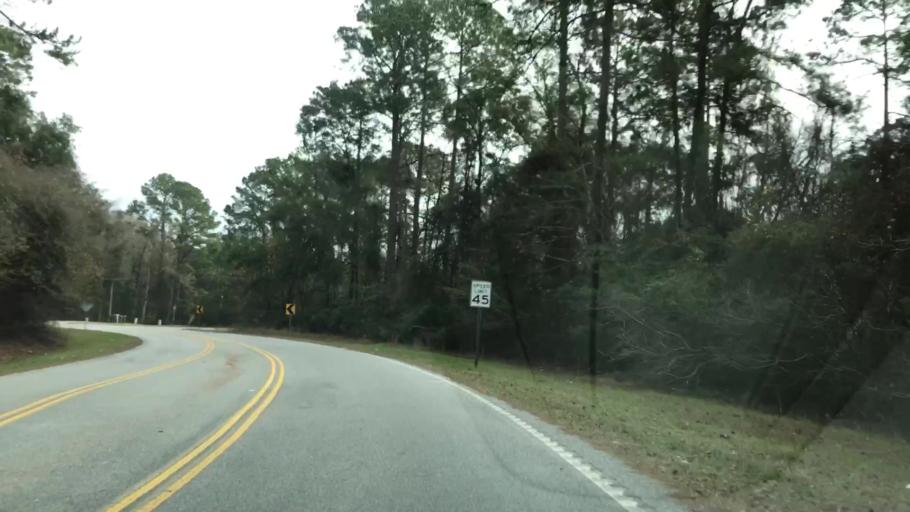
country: US
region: South Carolina
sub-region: Beaufort County
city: Burton
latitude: 32.4175
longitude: -80.7440
